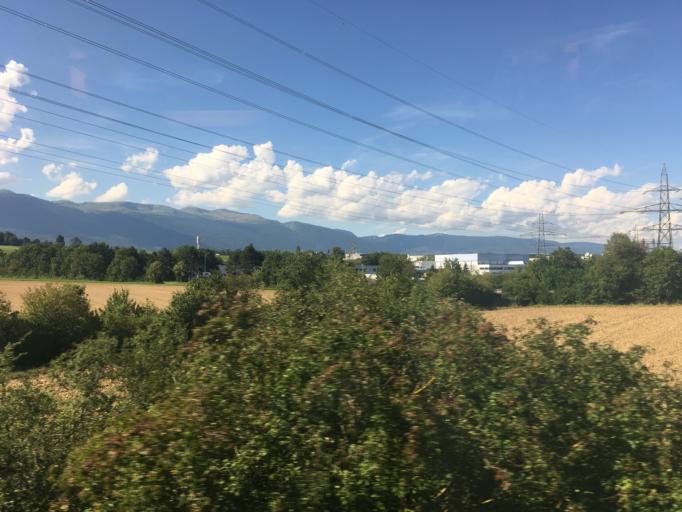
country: CH
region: Geneva
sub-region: Geneva
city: Satigny
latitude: 46.2197
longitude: 6.0497
